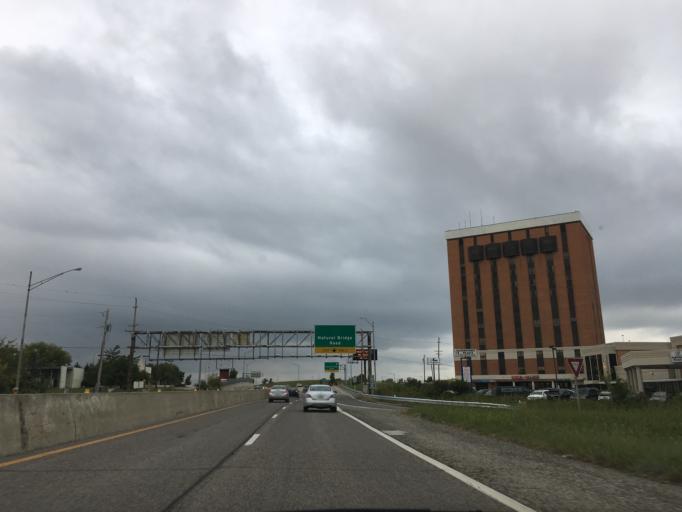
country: US
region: Missouri
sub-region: Saint Louis County
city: Saint Ann
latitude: 38.7451
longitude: -90.3947
